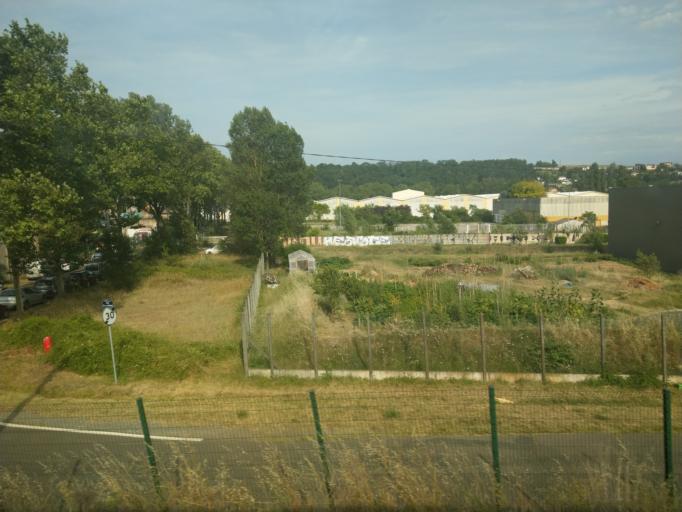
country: FR
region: Rhone-Alpes
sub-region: Departement du Rhone
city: Albigny-sur-Saone
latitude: 45.8544
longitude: 4.8312
